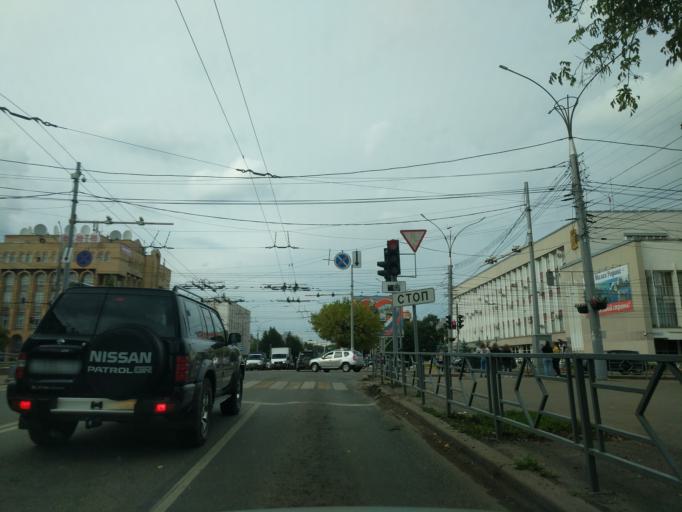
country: RU
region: Kirov
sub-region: Kirovo-Chepetskiy Rayon
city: Kirov
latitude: 58.5938
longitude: 49.6687
